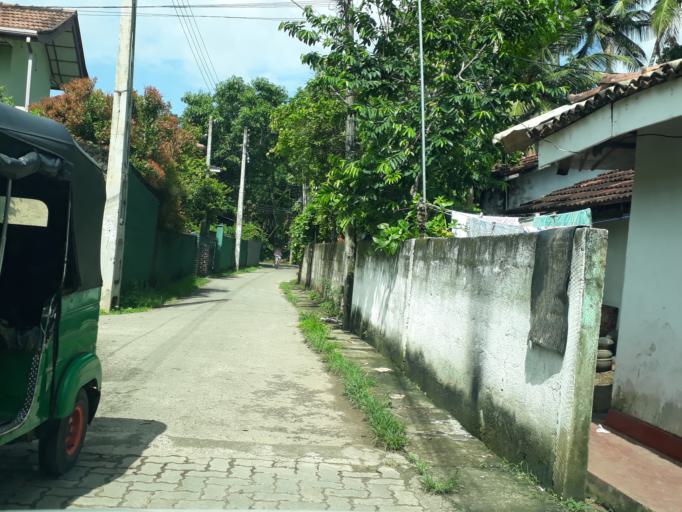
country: LK
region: Southern
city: Matara
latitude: 5.9517
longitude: 80.5266
